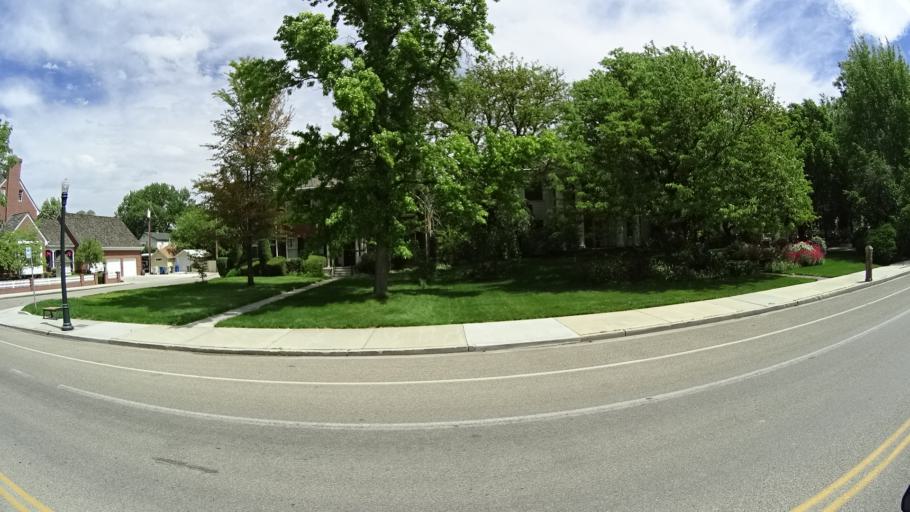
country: US
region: Idaho
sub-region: Ada County
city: Boise
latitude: 43.6059
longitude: -116.1800
